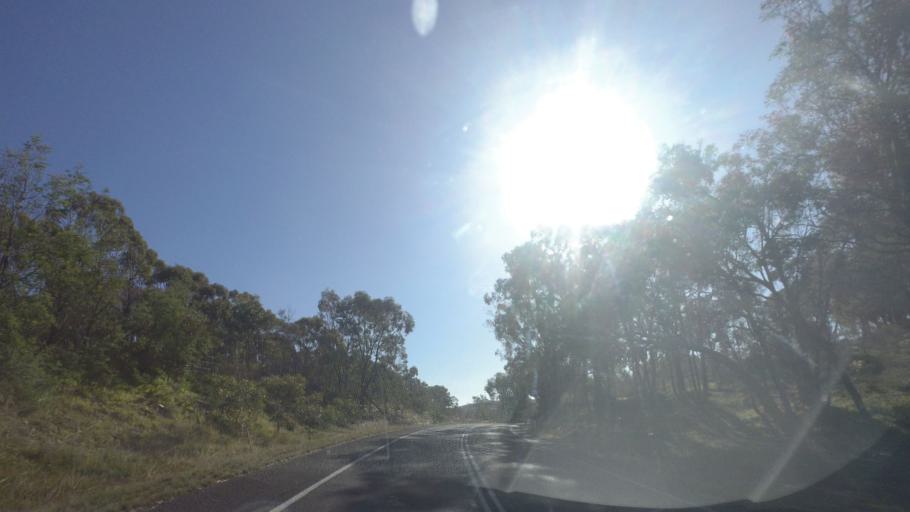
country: AU
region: Victoria
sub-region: Greater Bendigo
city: Kennington
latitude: -36.9173
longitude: 144.3350
